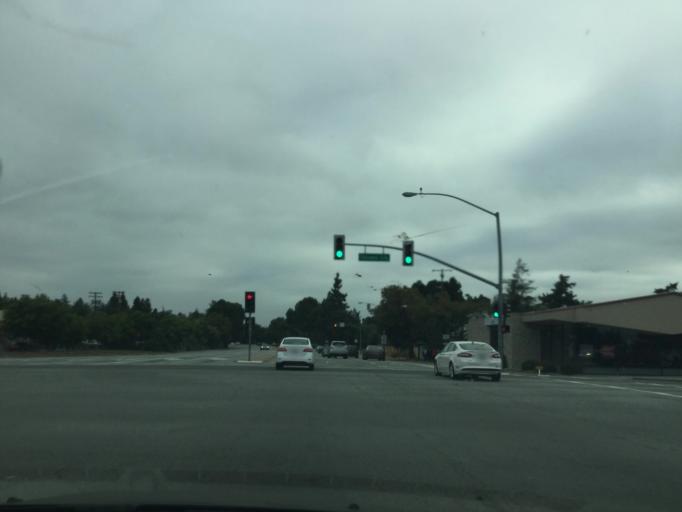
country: US
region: California
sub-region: Santa Clara County
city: Santa Clara
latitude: 37.3230
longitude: -121.9640
